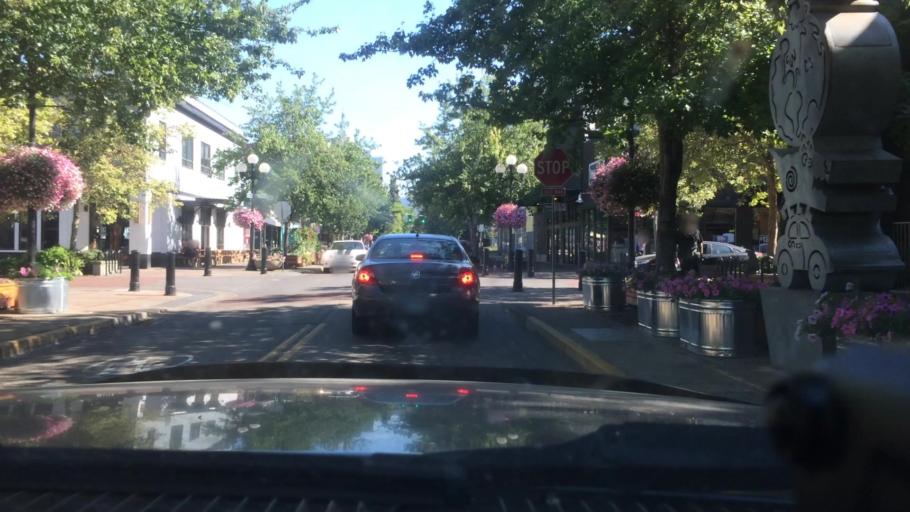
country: US
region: Oregon
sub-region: Lane County
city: Eugene
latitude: 44.0502
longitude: -123.0942
